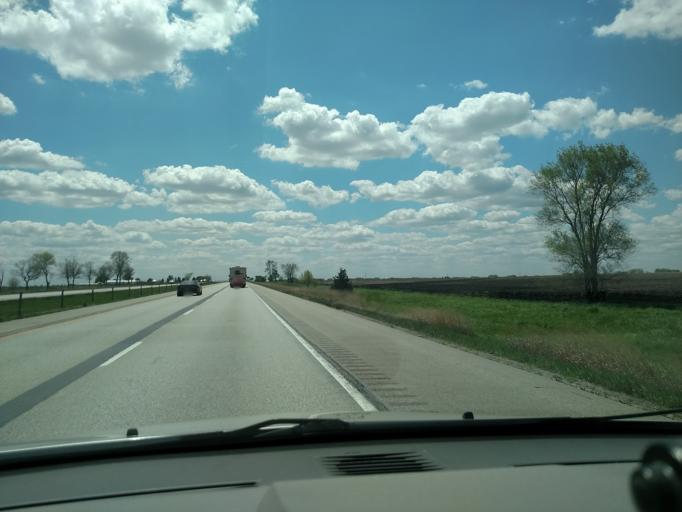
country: US
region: Iowa
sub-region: Polk County
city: Ankeny
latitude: 41.7859
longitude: -93.5707
